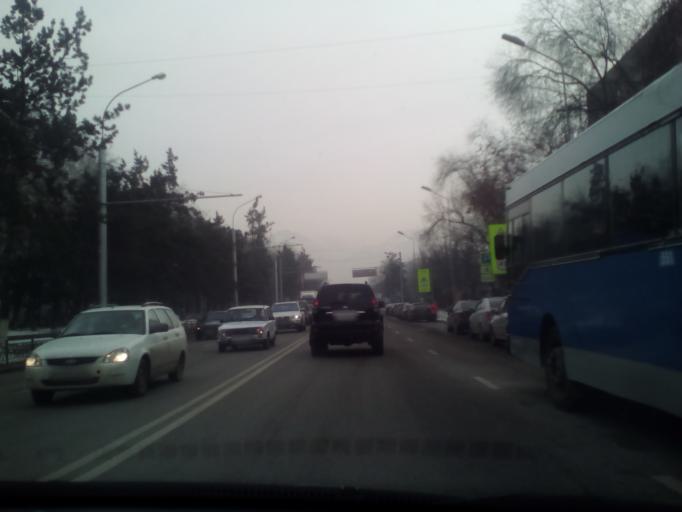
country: KZ
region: Almaty Qalasy
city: Almaty
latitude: 43.2386
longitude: 76.8297
